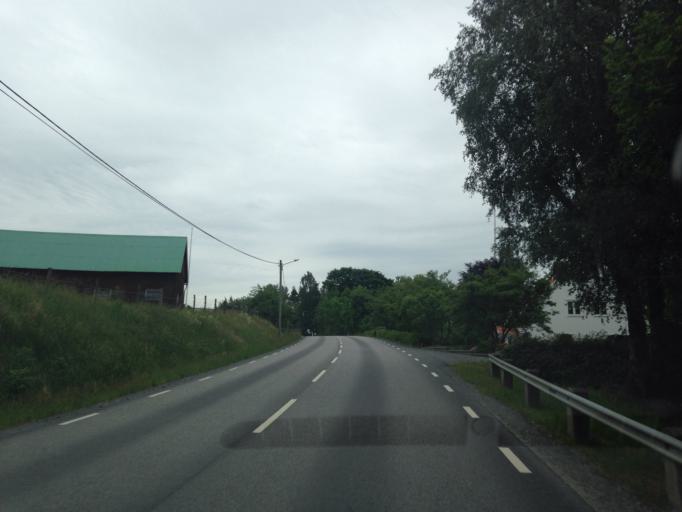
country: SE
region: Vaestra Goetaland
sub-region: Marks Kommun
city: Bua
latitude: 57.5085
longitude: 12.5477
